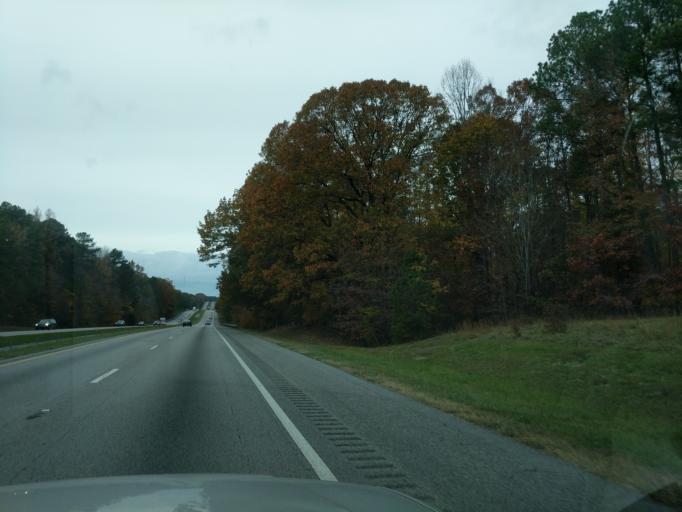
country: US
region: South Carolina
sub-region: Laurens County
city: Joanna
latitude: 34.4523
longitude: -81.7819
